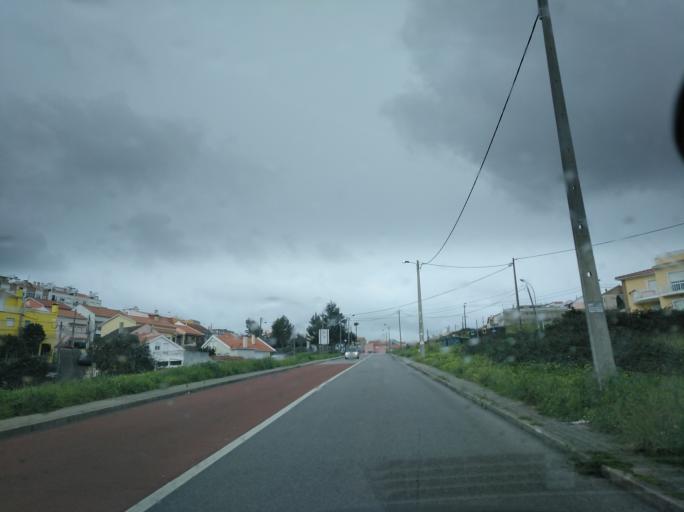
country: PT
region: Lisbon
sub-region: Odivelas
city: Canecas
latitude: 38.7969
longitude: -9.2262
